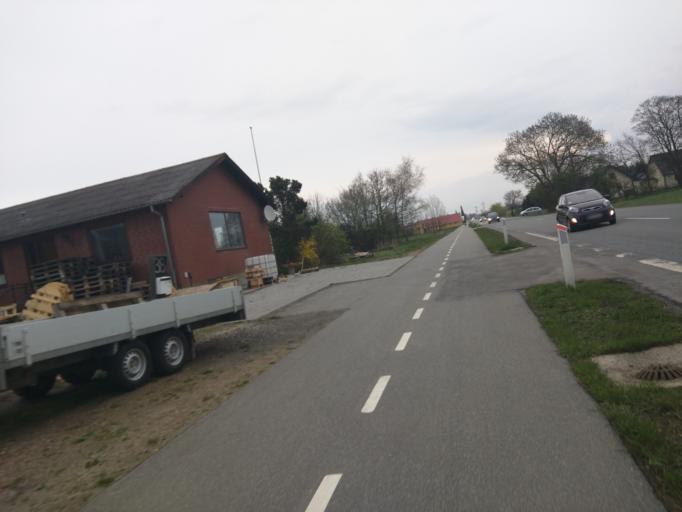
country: DK
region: Central Jutland
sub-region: Viborg Kommune
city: Viborg
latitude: 56.4702
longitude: 9.5365
